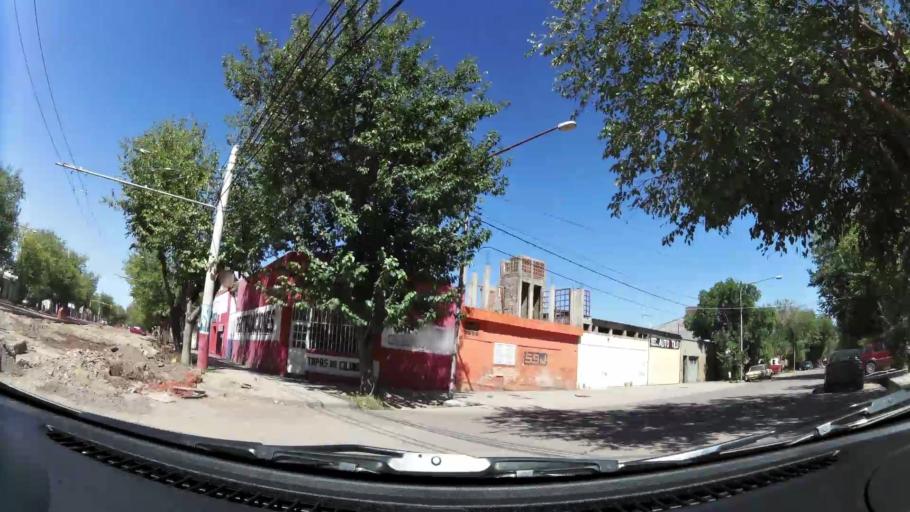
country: AR
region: Mendoza
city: Mendoza
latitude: -32.8918
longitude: -68.8051
